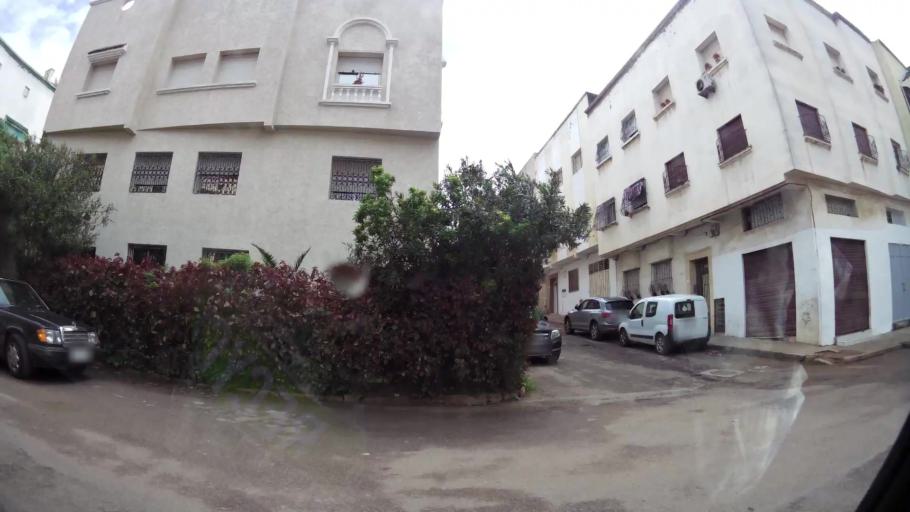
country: MA
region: Grand Casablanca
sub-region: Casablanca
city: Casablanca
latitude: 33.5401
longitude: -7.6784
